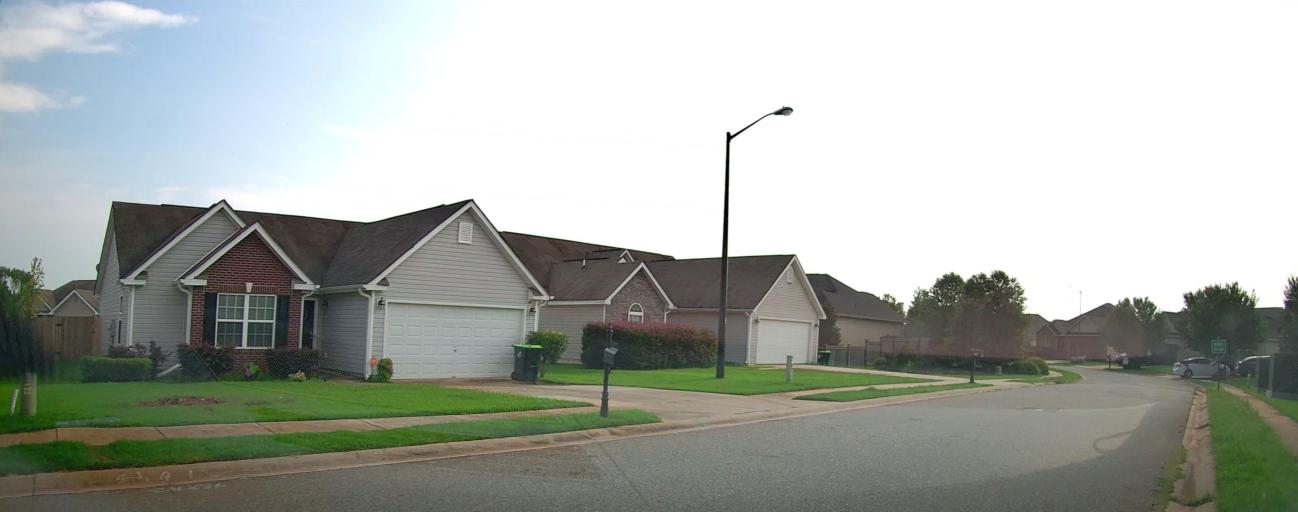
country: US
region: Georgia
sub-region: Houston County
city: Centerville
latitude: 32.6291
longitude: -83.7183
